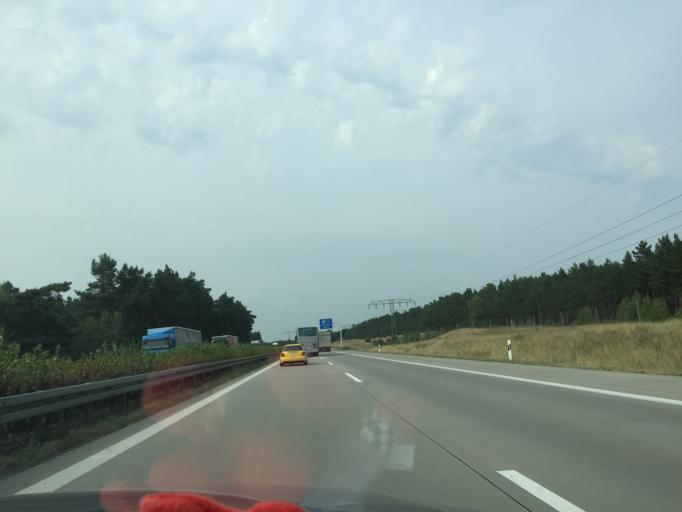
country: DE
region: Brandenburg
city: Schwerin
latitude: 52.1439
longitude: 13.6489
